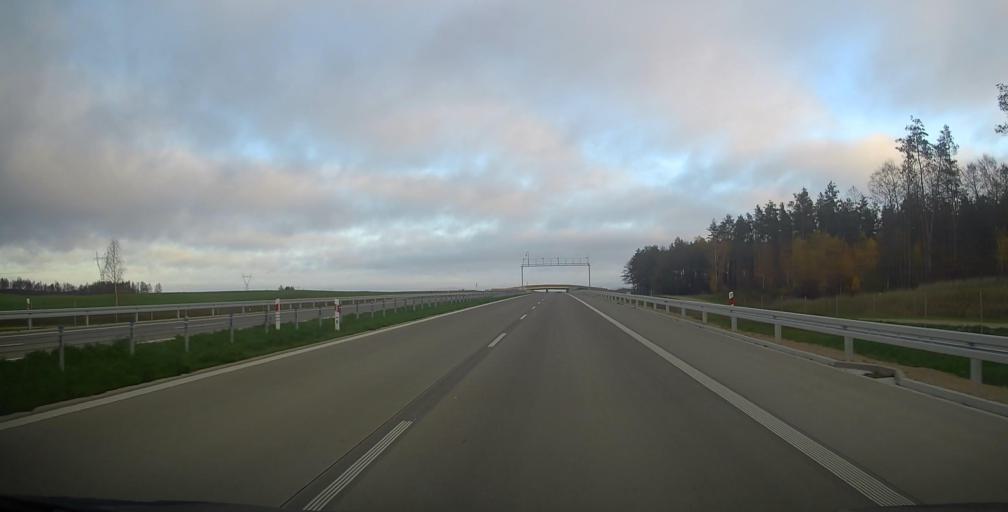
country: PL
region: Podlasie
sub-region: Powiat grajewski
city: Szczuczyn
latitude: 53.6472
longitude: 22.2942
